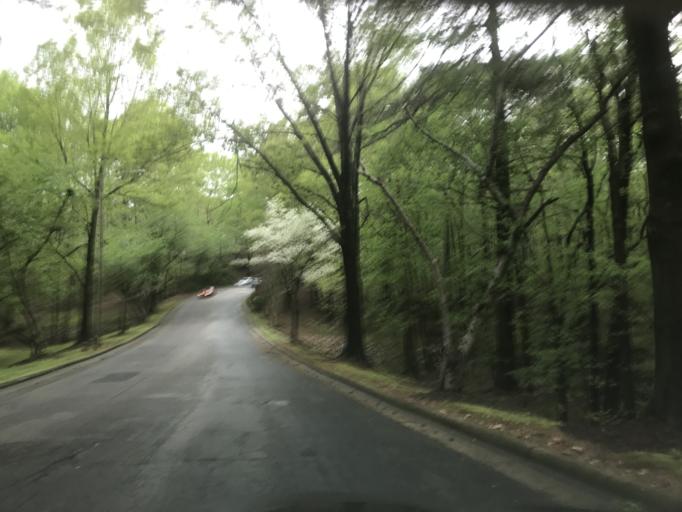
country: US
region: North Carolina
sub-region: Wake County
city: West Raleigh
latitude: 35.7575
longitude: -78.7008
